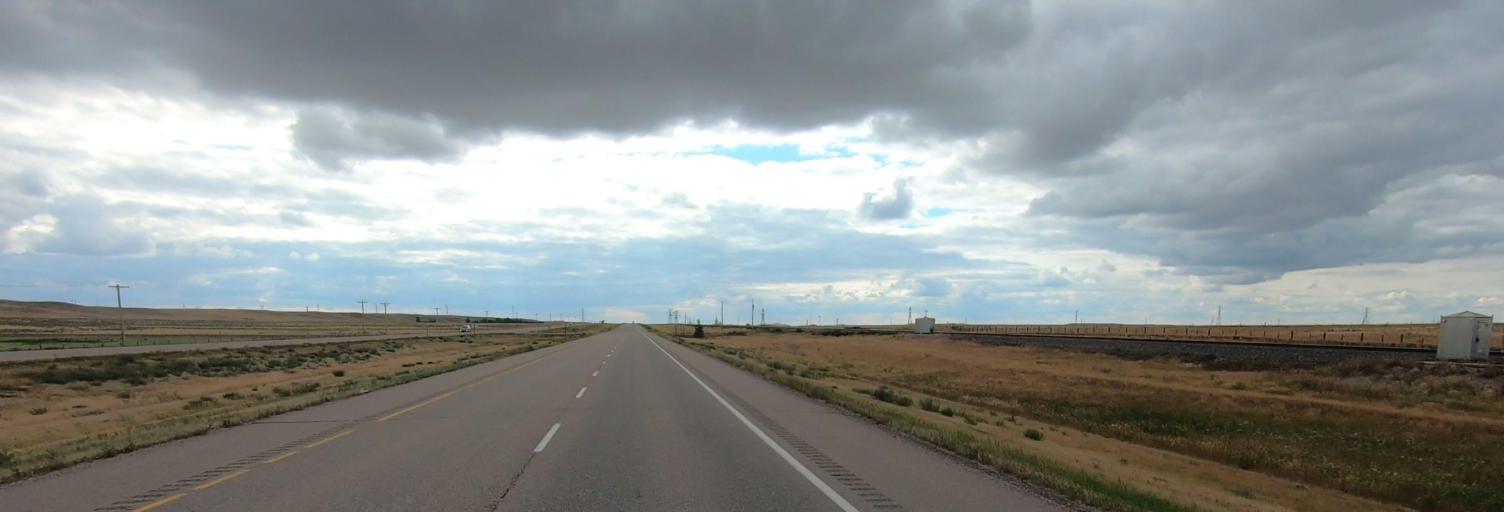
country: CA
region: Alberta
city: Medicine Hat
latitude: 49.9820
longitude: -110.4565
